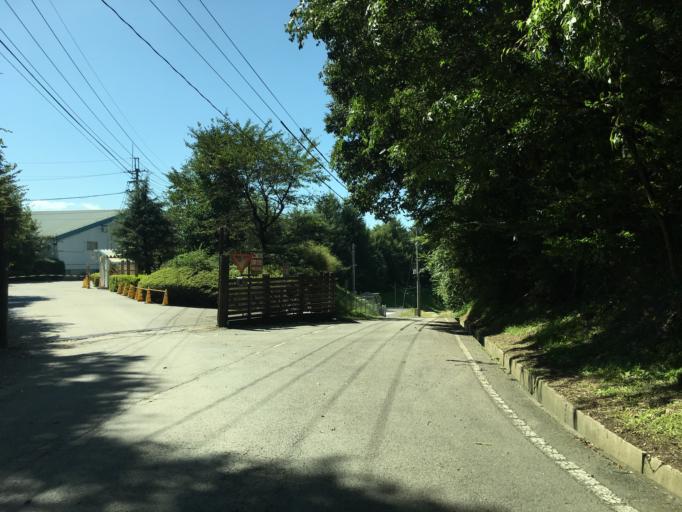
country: JP
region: Fukushima
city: Ishikawa
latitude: 37.2052
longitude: 140.5764
